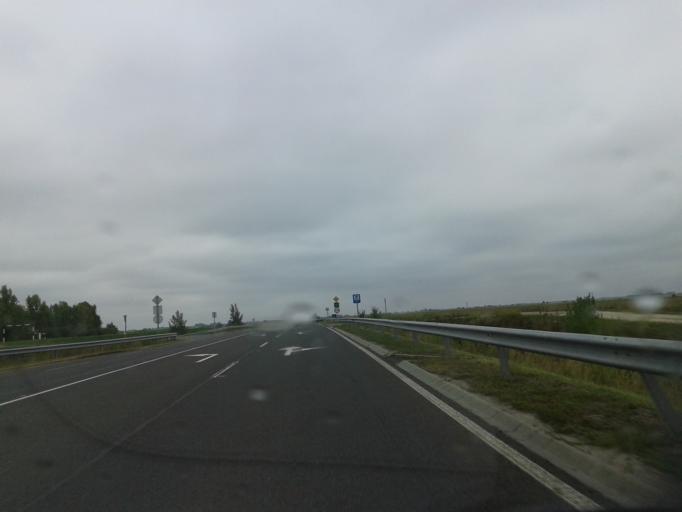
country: HU
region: Tolna
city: Bolcske
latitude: 46.7551
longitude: 19.0092
